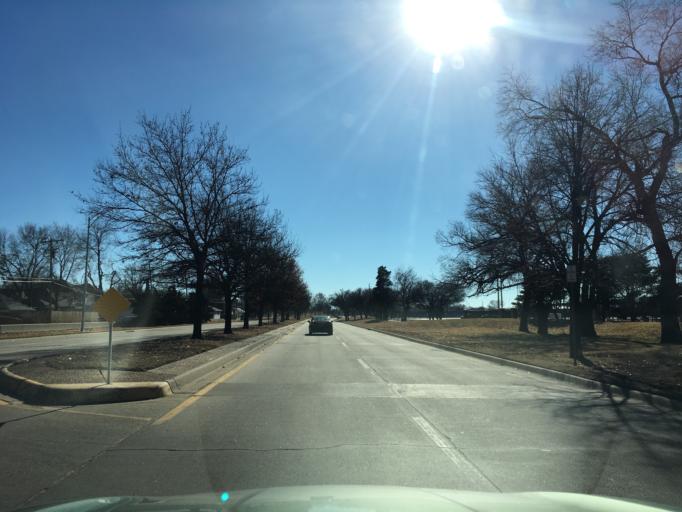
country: US
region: Kansas
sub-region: Sedgwick County
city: Wichita
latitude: 37.6843
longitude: -97.3078
